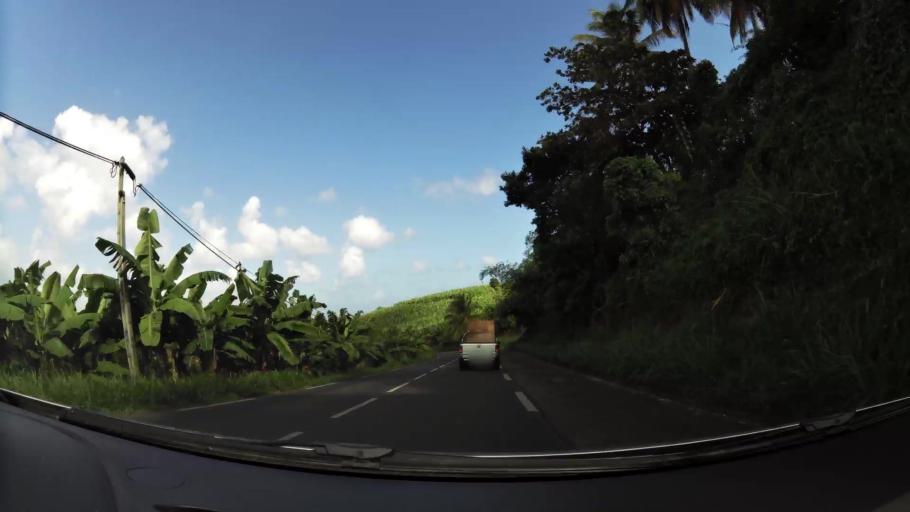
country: MQ
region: Martinique
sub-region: Martinique
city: Le Lorrain
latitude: 14.8411
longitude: -61.0809
